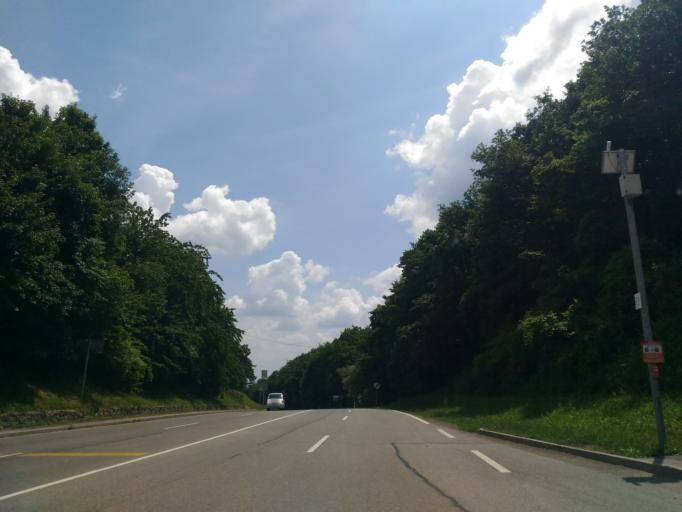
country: HU
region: Baranya
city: Pecs
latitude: 46.1369
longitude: 18.2504
